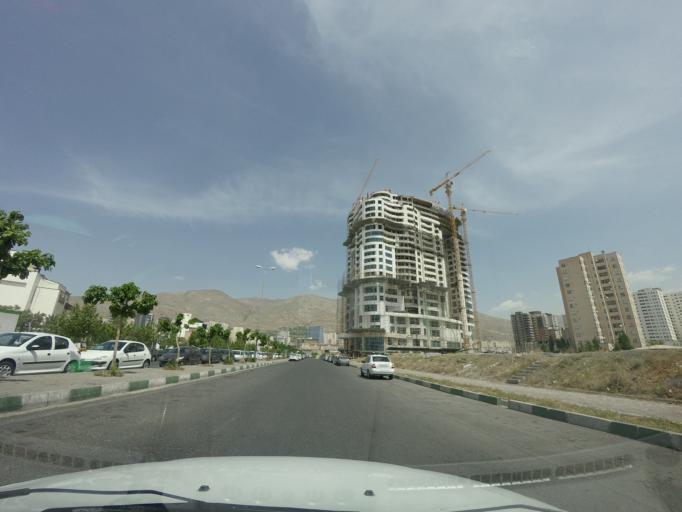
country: IR
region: Tehran
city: Shahr-e Qods
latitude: 35.7446
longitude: 51.2225
